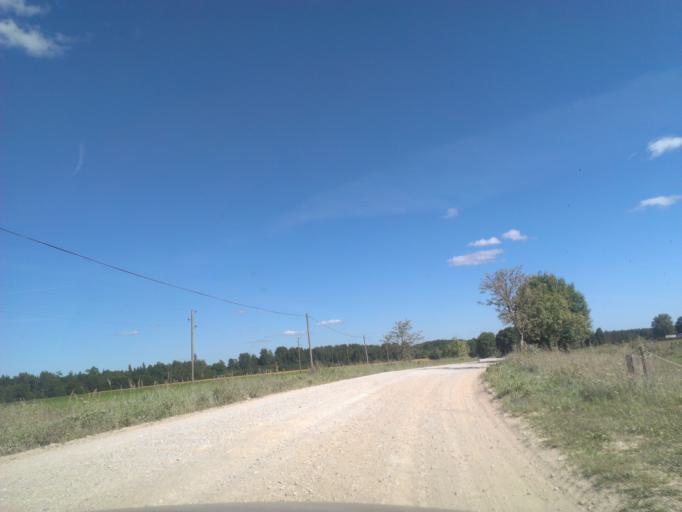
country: LV
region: Malpils
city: Malpils
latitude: 57.0158
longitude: 24.9967
